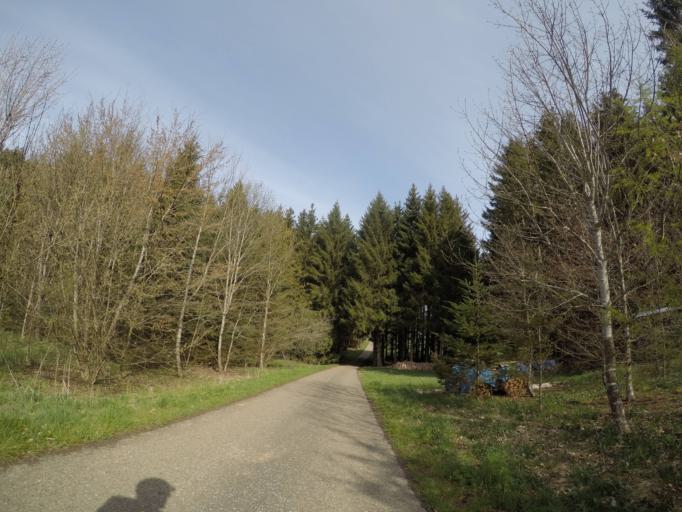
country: DE
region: Baden-Wuerttemberg
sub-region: Regierungsbezirk Stuttgart
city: Hohenstadt
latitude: 48.5214
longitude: 9.6724
